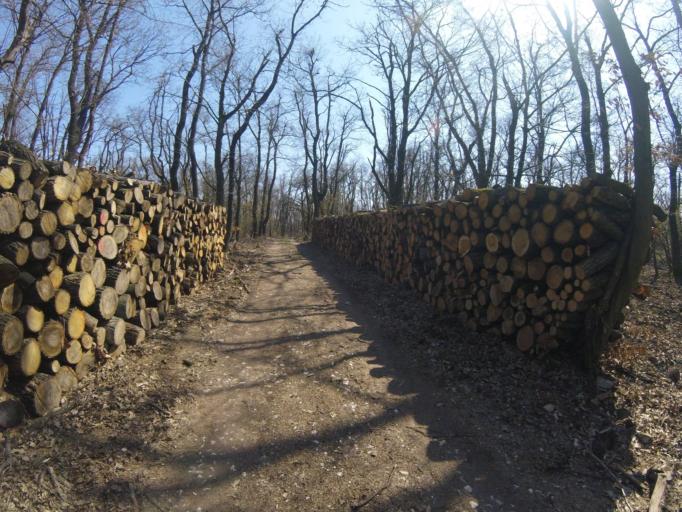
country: HU
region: Pest
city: Budakeszi
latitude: 47.5466
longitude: 18.8933
